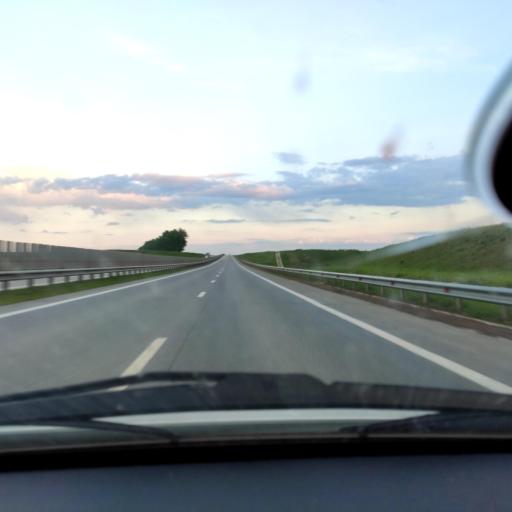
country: RU
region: Bashkortostan
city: Kushnarenkovo
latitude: 55.1050
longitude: 55.2355
